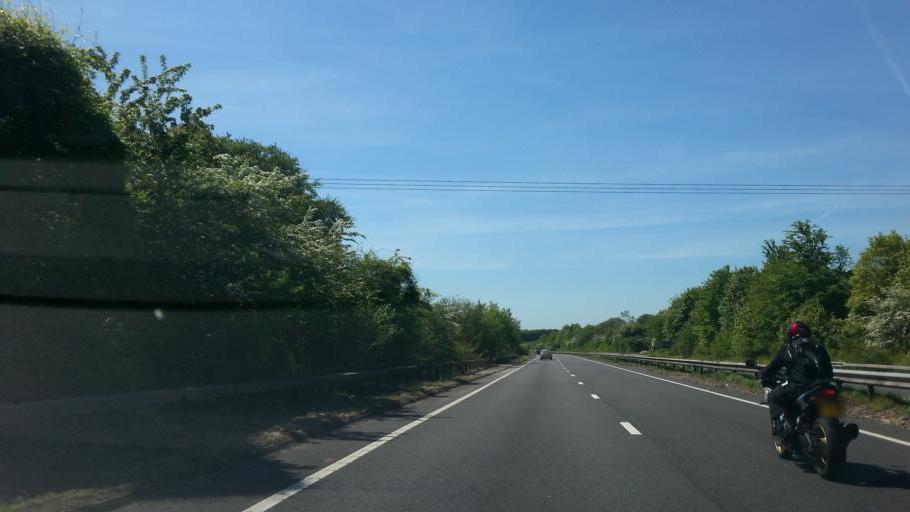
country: GB
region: England
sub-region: Hampshire
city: Overton
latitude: 51.1902
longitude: -1.2560
